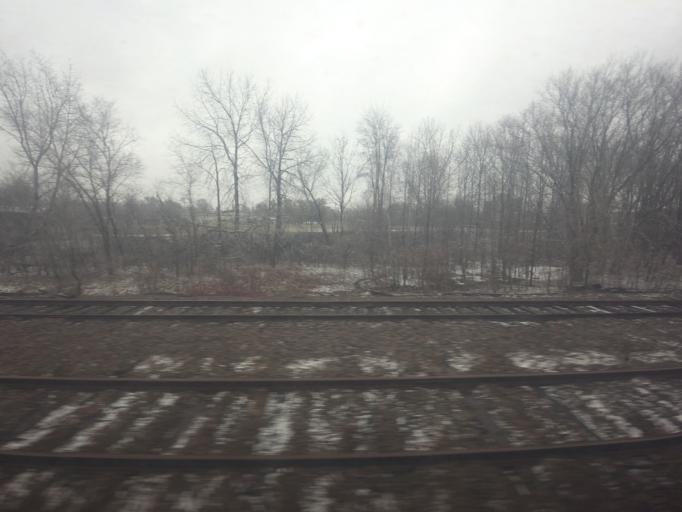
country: CA
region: Ontario
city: Brockville
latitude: 44.5958
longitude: -75.6886
